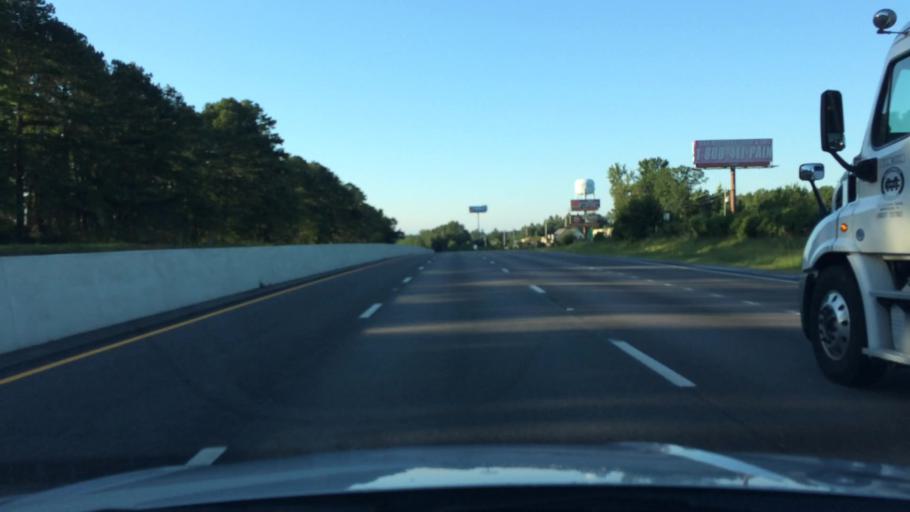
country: US
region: South Carolina
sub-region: Calhoun County
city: Oak Grove
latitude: 33.8328
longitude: -81.0210
